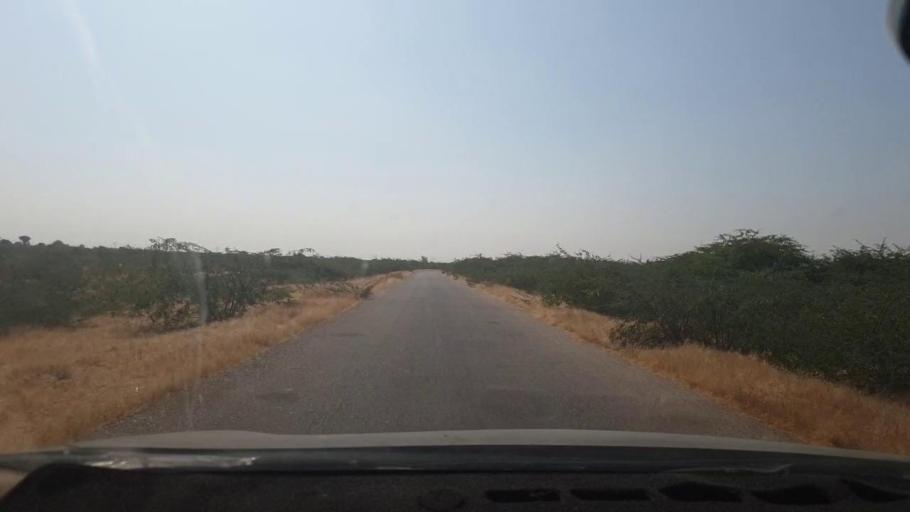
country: PK
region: Sindh
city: Malir Cantonment
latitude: 25.1596
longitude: 67.1506
